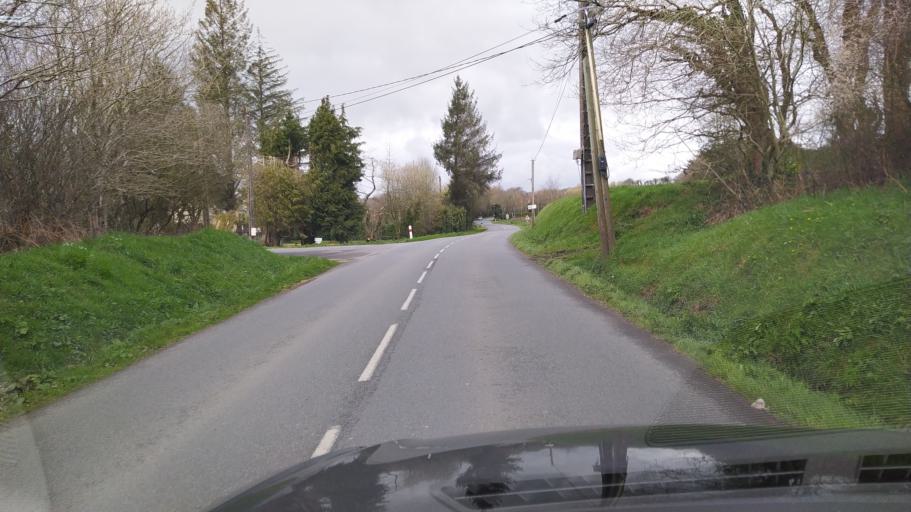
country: FR
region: Brittany
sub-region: Departement du Finistere
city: Bodilis
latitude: 48.5173
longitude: -4.1137
